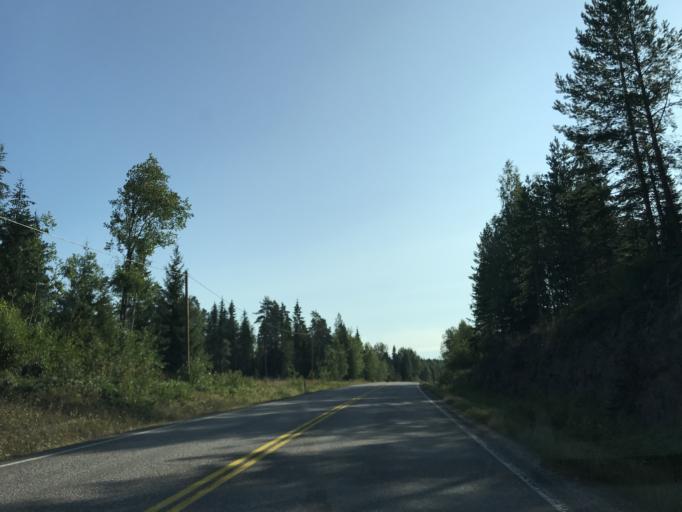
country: FI
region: Uusimaa
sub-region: Porvoo
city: Pukkila
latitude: 60.7806
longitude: 25.5804
